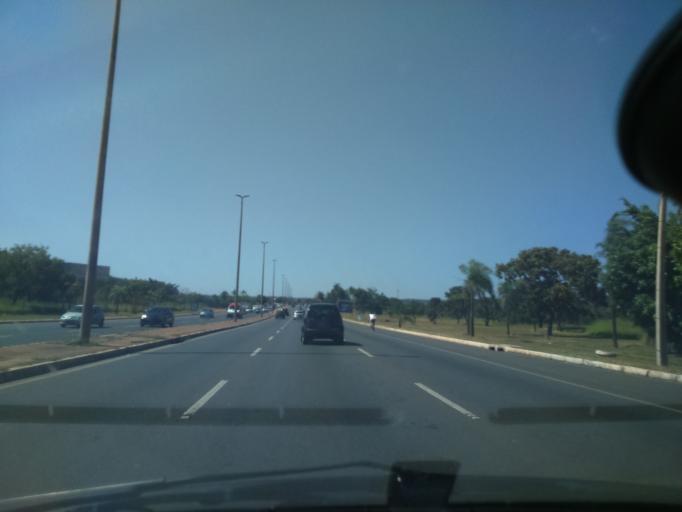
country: BR
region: Federal District
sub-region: Brasilia
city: Brasilia
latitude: -15.8091
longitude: -47.8481
